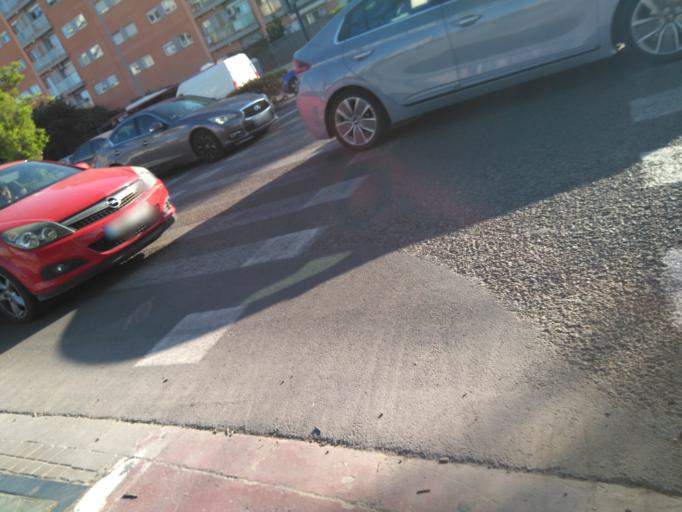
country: ES
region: Valencia
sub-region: Provincia de Valencia
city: Tavernes Blanques
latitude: 39.4974
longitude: -0.3846
